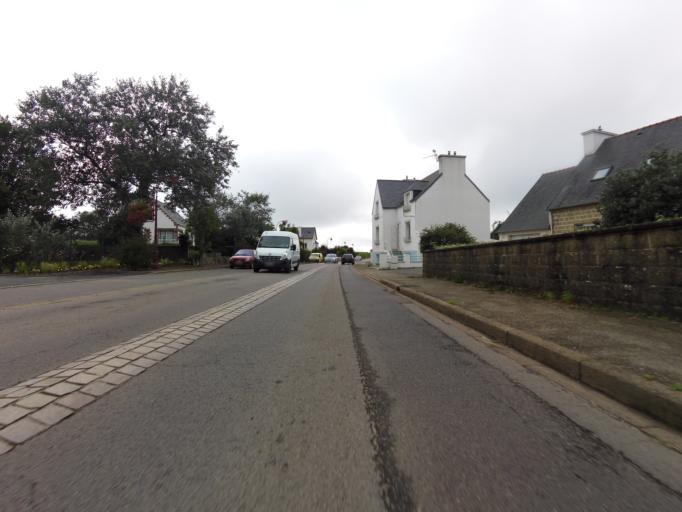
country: FR
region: Brittany
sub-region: Departement du Finistere
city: Plouhinec
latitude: 48.0133
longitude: -4.4814
